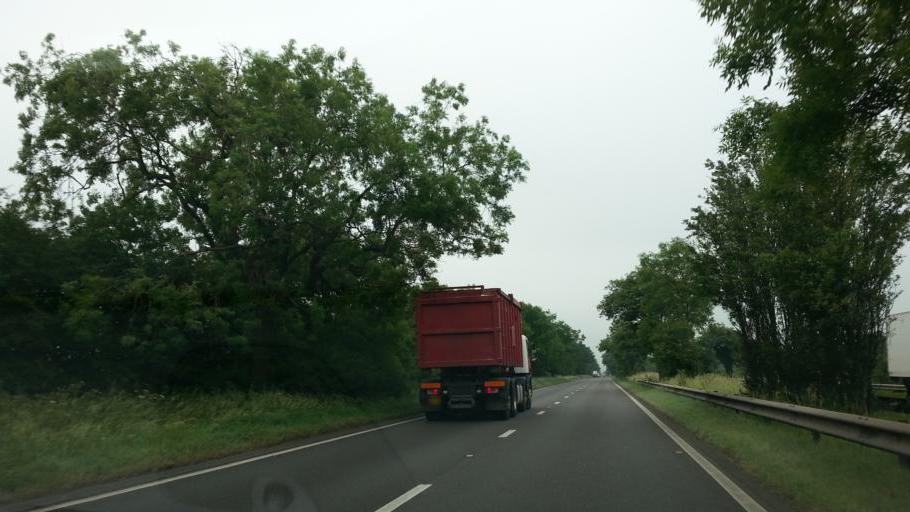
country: GB
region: England
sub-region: Leicestershire
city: Queniborough
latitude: 52.7672
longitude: -1.0532
